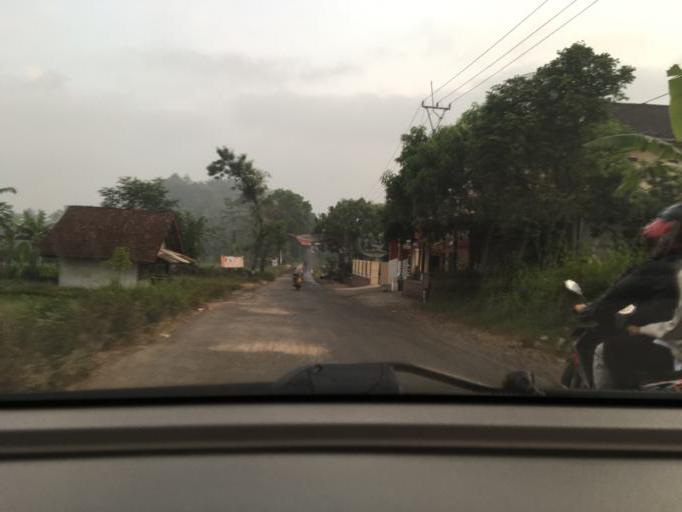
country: ID
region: West Java
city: Pasireurih
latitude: -7.1822
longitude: 108.1970
